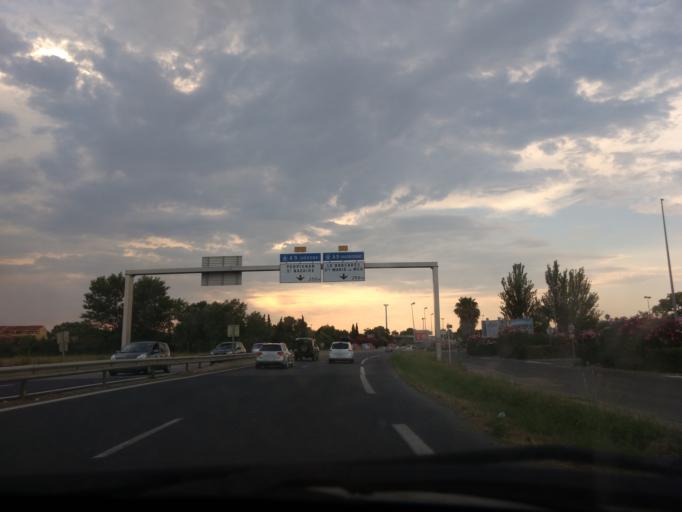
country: FR
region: Languedoc-Roussillon
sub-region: Departement des Pyrenees-Orientales
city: Canet-en-Roussillon
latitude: 42.6997
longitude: 3.0201
